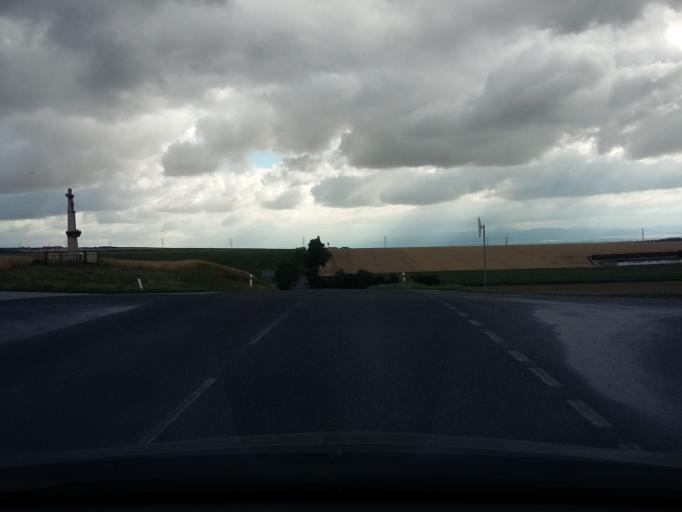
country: SK
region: Trnavsky
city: Vrbove
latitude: 48.5903
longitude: 17.6688
